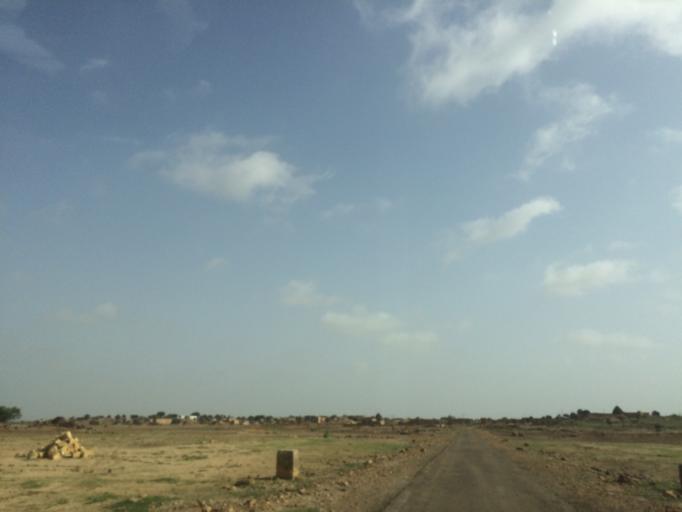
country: IN
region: Rajasthan
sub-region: Jaisalmer
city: Jaisalmer
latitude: 26.7643
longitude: 70.6800
